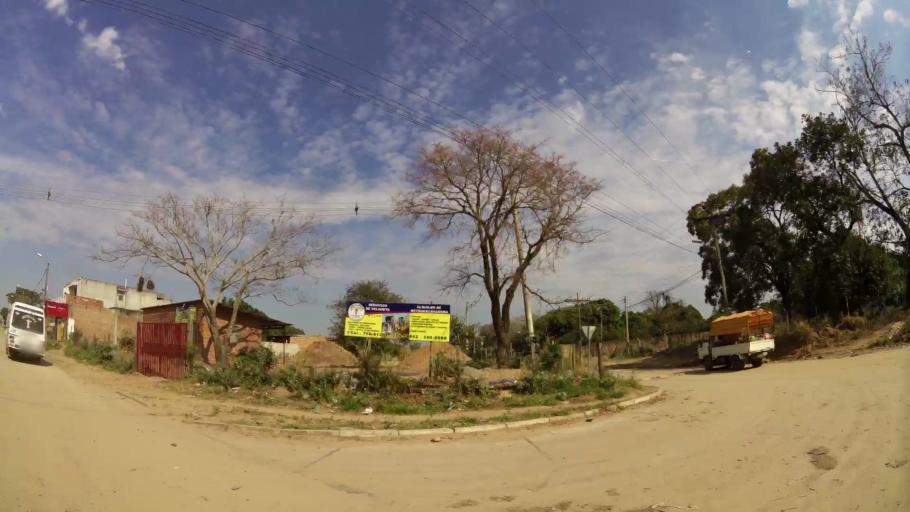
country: BO
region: Santa Cruz
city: Santa Cruz de la Sierra
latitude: -17.7199
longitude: -63.1531
